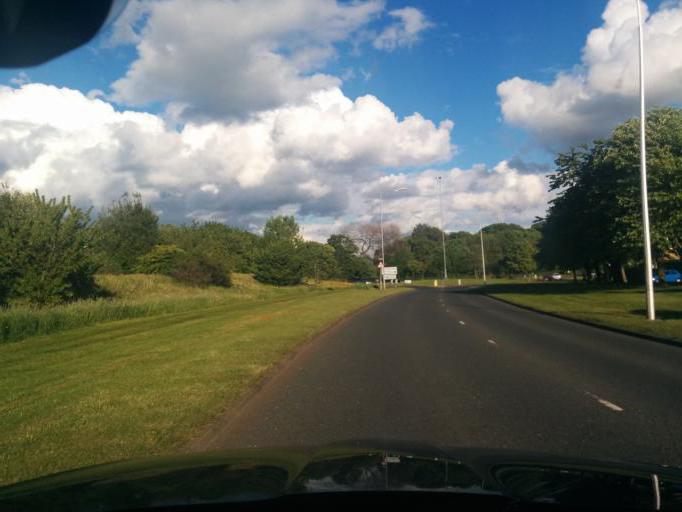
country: GB
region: England
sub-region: Northumberland
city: Cramlington
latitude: 55.0832
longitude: -1.5898
